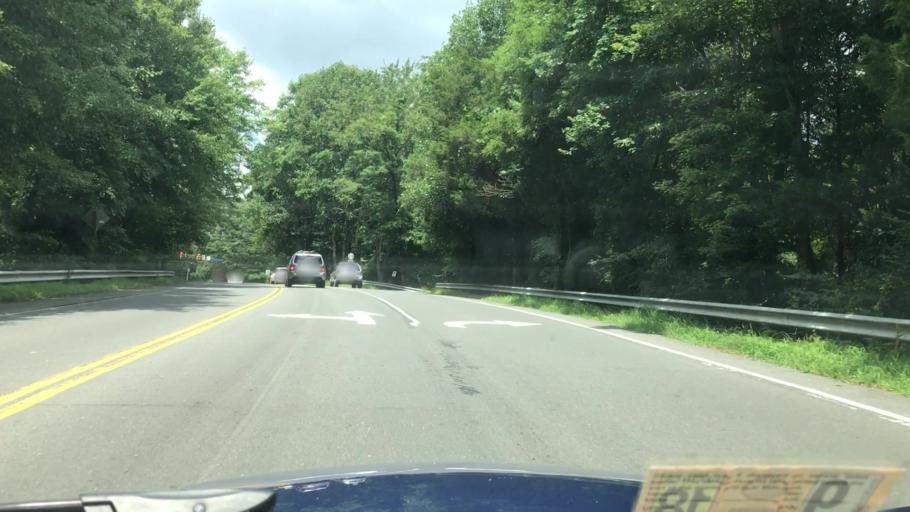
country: US
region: Virginia
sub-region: Fairfax County
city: Wolf Trap
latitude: 38.9196
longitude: -77.3038
